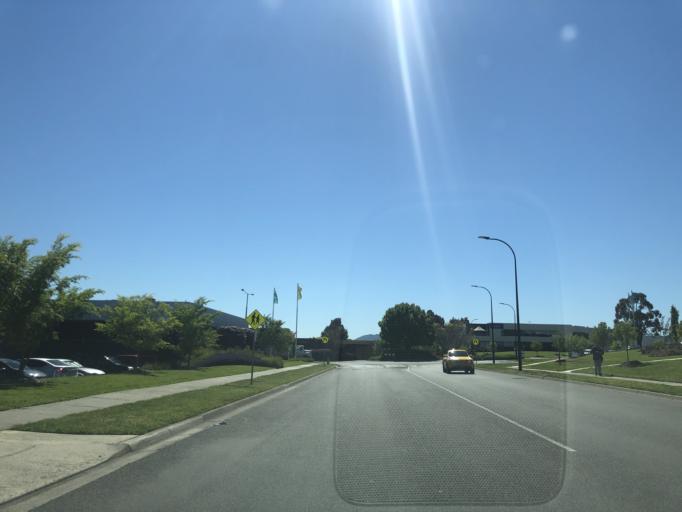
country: AU
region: Victoria
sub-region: Knox
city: Scoresby
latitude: -37.9029
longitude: 145.2203
